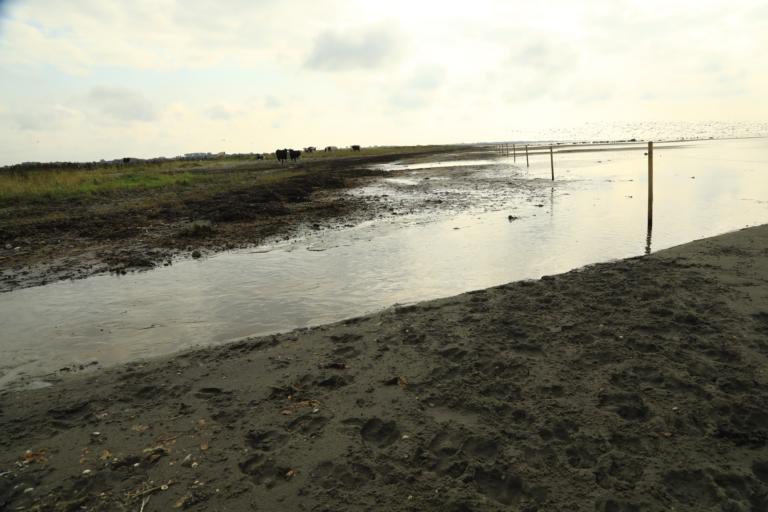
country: SE
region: Halland
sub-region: Varbergs Kommun
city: Tvaaker
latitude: 57.0018
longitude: 12.3524
